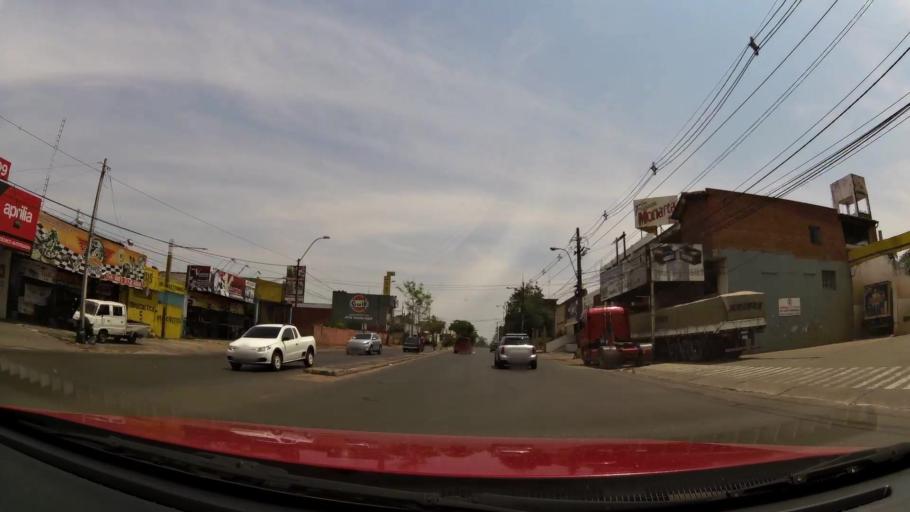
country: PY
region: Central
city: Lambare
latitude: -25.3161
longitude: -57.5750
